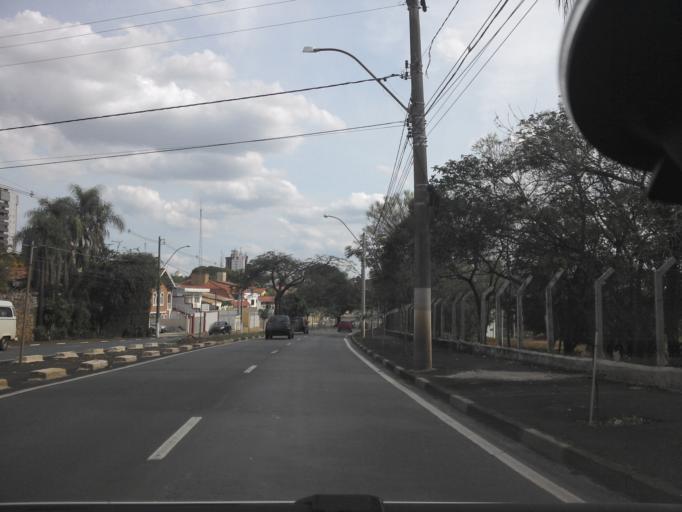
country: BR
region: Sao Paulo
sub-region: Campinas
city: Campinas
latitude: -22.8815
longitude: -47.0756
